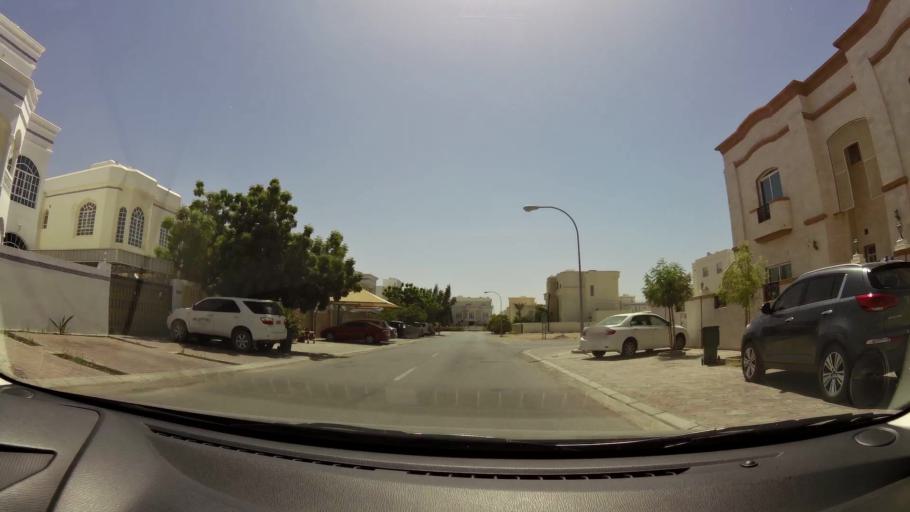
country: OM
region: Muhafazat Masqat
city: Bawshar
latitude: 23.5999
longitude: 58.3630
